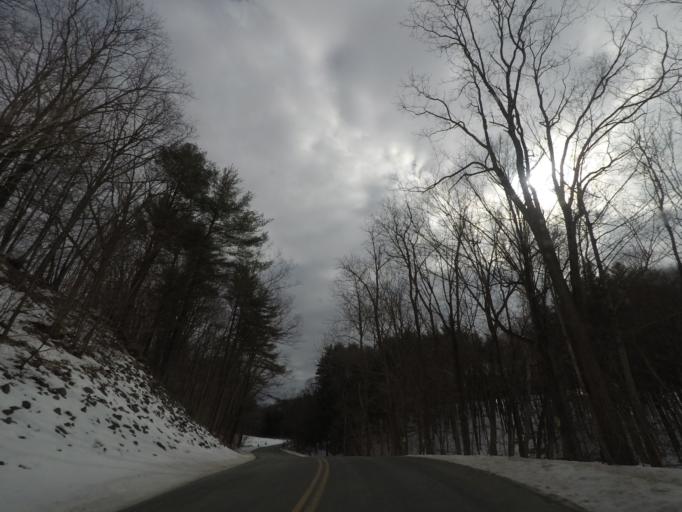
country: US
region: New York
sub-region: Rensselaer County
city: Hoosick Falls
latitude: 42.8838
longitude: -73.4180
